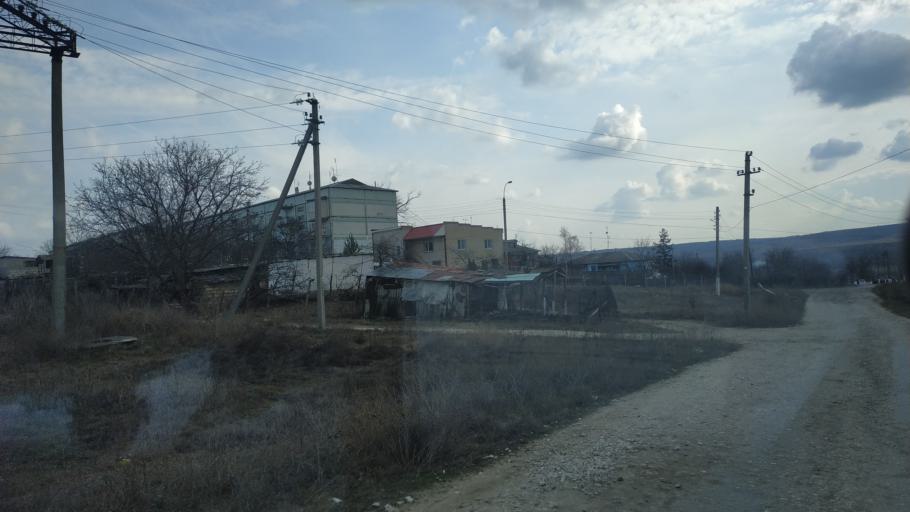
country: MD
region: Anenii Noi
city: Anenii Noi
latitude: 46.8932
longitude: 29.2807
